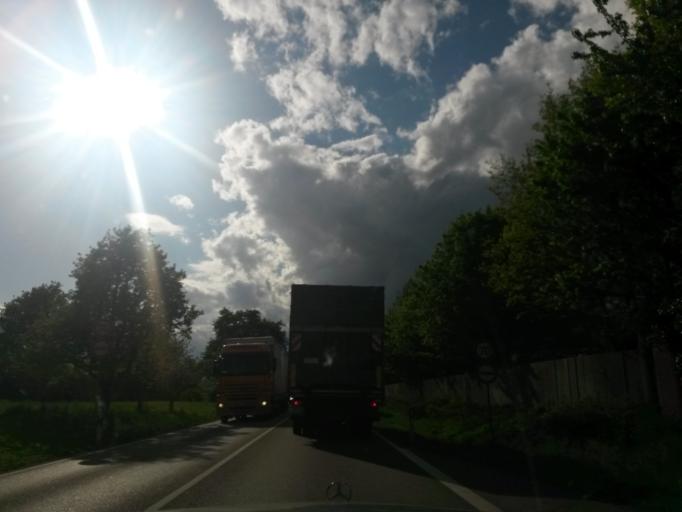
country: DE
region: Baden-Wuerttemberg
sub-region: Regierungsbezirk Stuttgart
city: Westhausen
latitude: 48.8868
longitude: 10.1580
